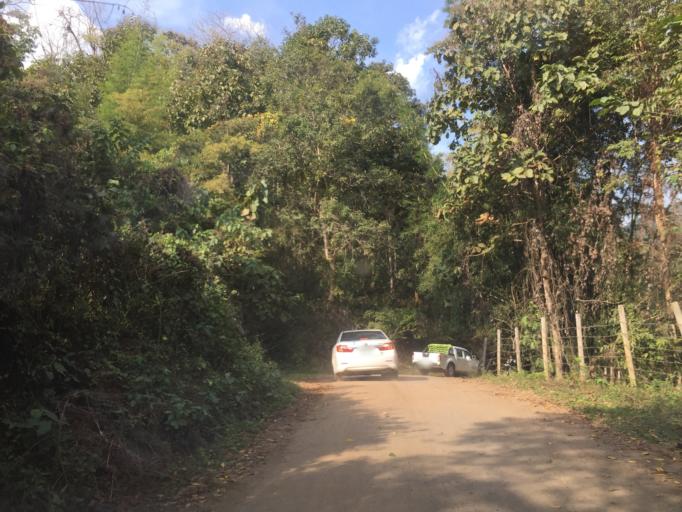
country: TH
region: Chiang Mai
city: Samoeng
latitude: 19.0083
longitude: 98.7300
